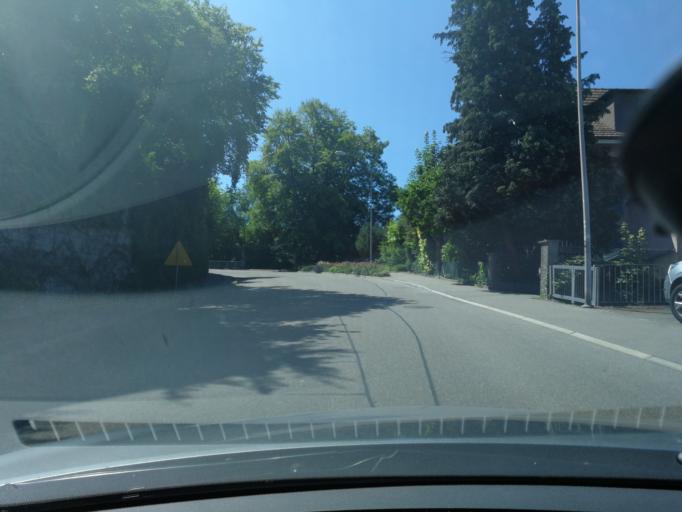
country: CH
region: Zurich
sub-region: Bezirk Meilen
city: Erlenbach / links des Dorfbachs oberhalb Bahnlinie
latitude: 47.2964
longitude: 8.6008
